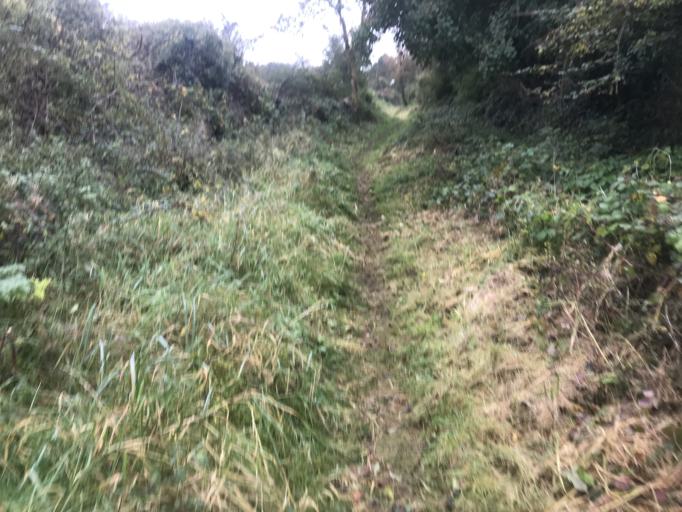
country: IE
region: Connaught
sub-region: County Galway
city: Gaillimh
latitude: 53.2971
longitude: -9.0512
